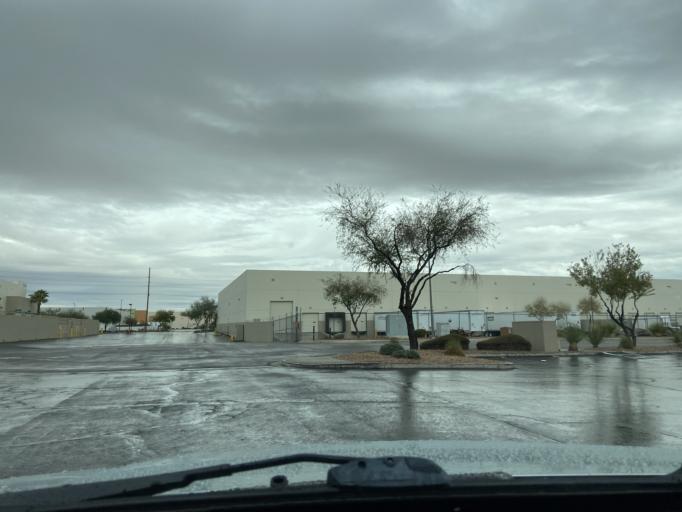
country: US
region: Nevada
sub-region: Clark County
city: Sunrise Manor
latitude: 36.2360
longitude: -115.1005
